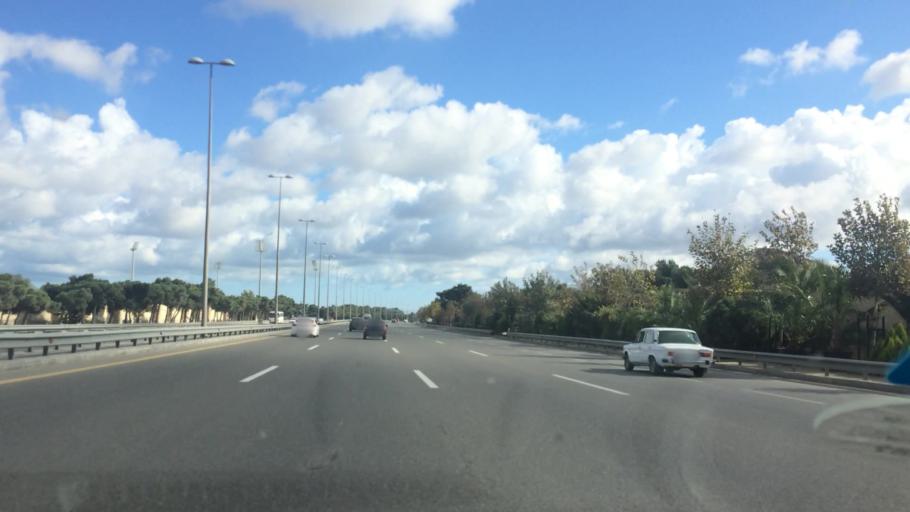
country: AZ
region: Baki
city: Biny Selo
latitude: 40.4614
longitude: 50.0795
